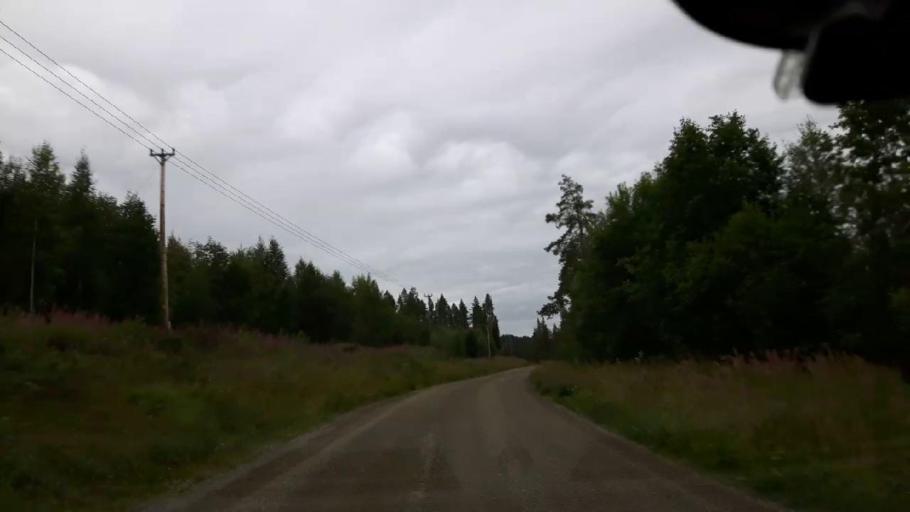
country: SE
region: Jaemtland
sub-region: Braecke Kommun
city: Braecke
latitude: 63.0112
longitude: 15.3799
